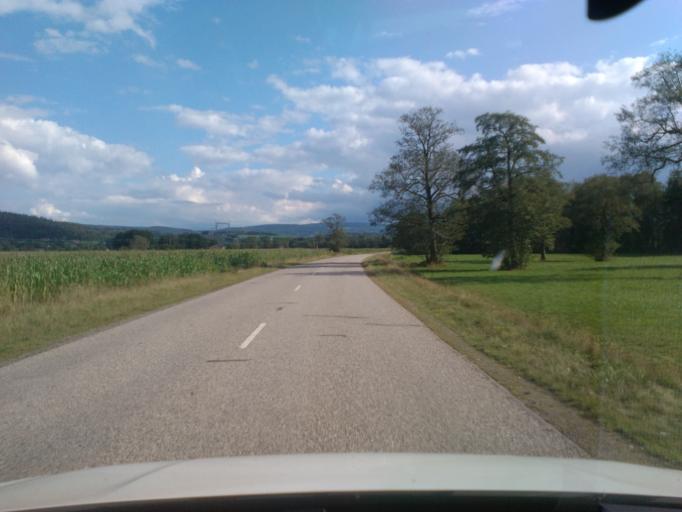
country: FR
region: Lorraine
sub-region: Departement des Vosges
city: Corcieux
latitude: 48.1947
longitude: 6.8803
